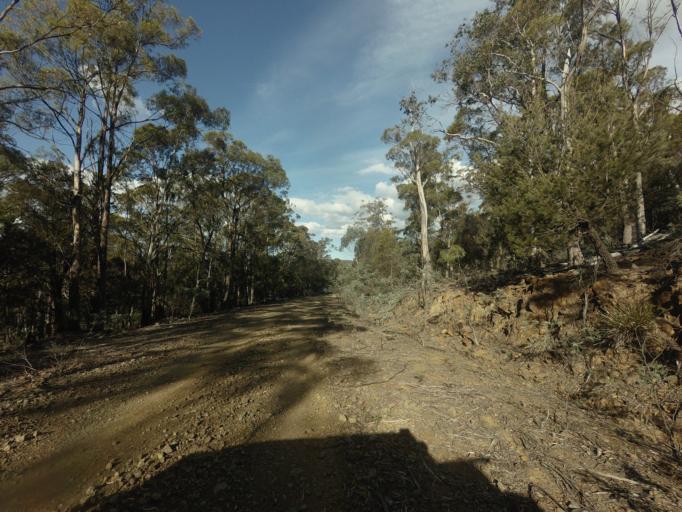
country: AU
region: Tasmania
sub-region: Break O'Day
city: St Helens
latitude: -41.8374
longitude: 148.0796
